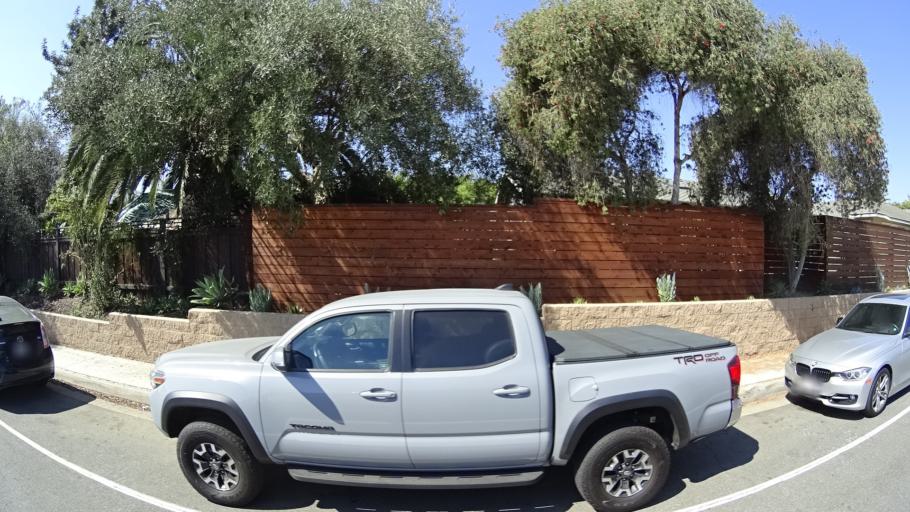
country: US
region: California
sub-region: Orange County
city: San Clemente
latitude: 33.4449
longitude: -117.6429
